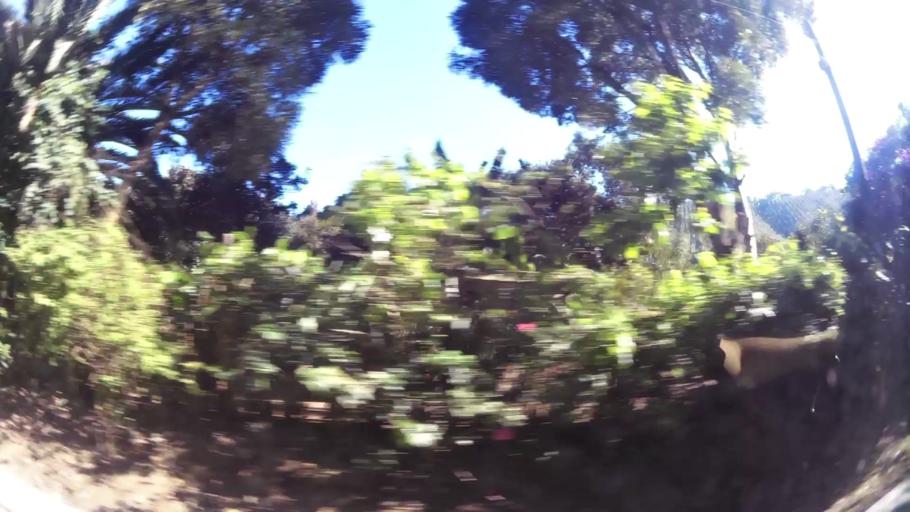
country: GT
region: Sacatepequez
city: Santa Lucia Milpas Altas
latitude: 14.5617
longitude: -90.7045
